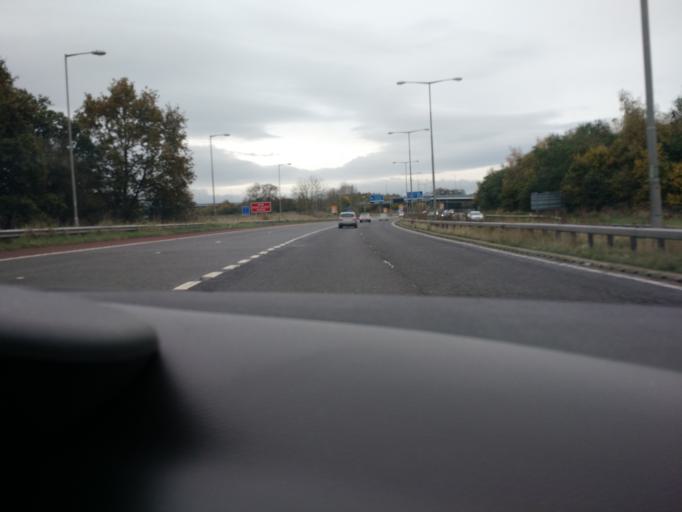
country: GB
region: England
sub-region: Lancashire
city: Goosnargh
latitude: 53.8053
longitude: -2.7058
